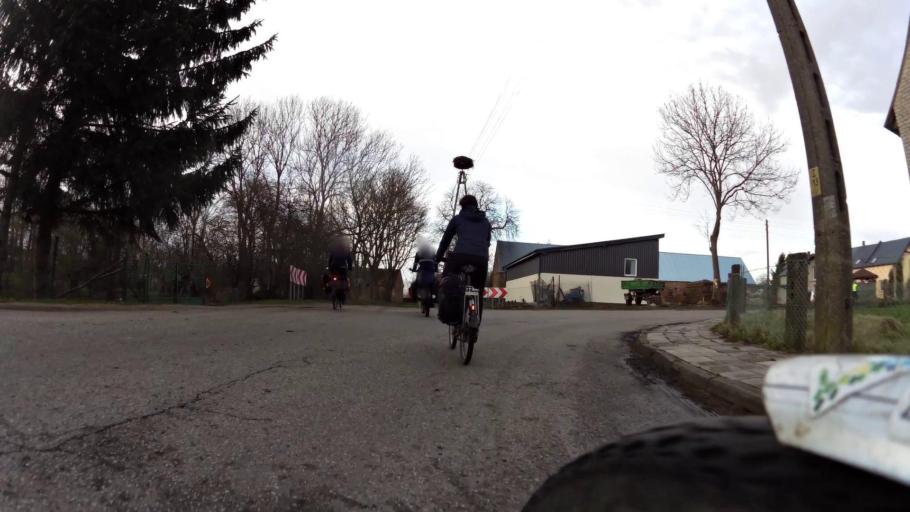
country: PL
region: West Pomeranian Voivodeship
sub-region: Powiat kamienski
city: Kamien Pomorski
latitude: 53.9221
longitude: 14.7594
